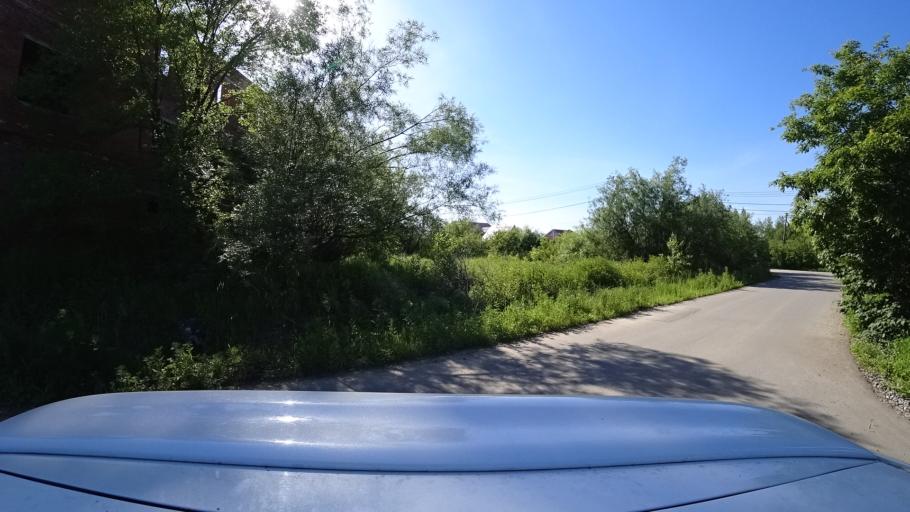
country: RU
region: Khabarovsk Krai
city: Topolevo
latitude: 48.5439
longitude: 135.1788
